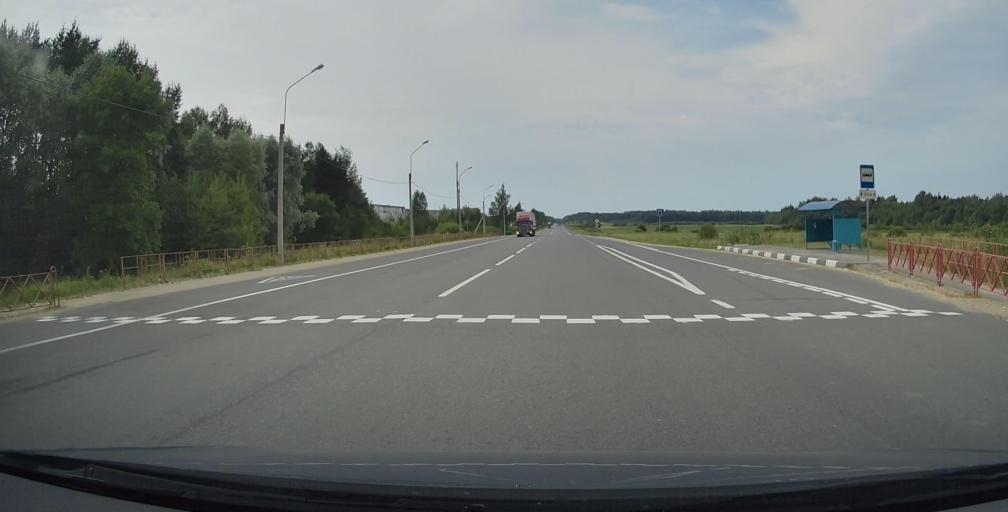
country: RU
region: Jaroslavl
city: Pesochnoye
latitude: 57.9869
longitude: 39.1133
